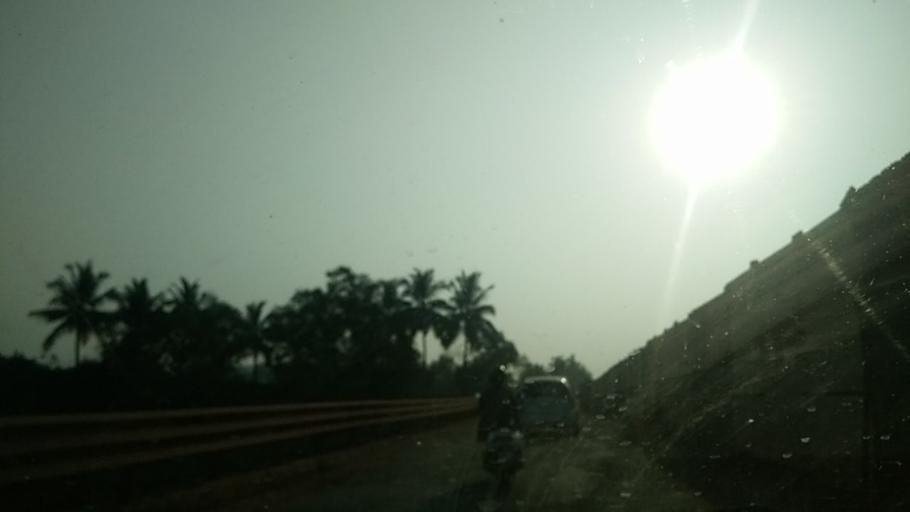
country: IN
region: Goa
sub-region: North Goa
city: Mapuca
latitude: 15.5866
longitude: 73.8194
